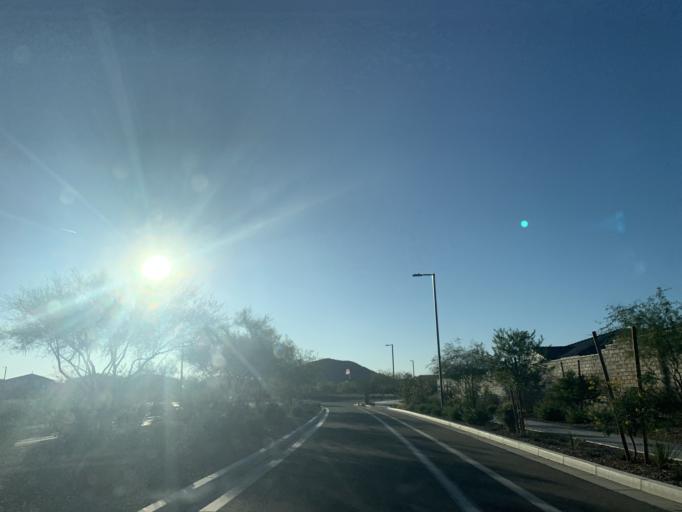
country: US
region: Arizona
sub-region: Maricopa County
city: Cave Creek
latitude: 33.6890
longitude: -112.0184
